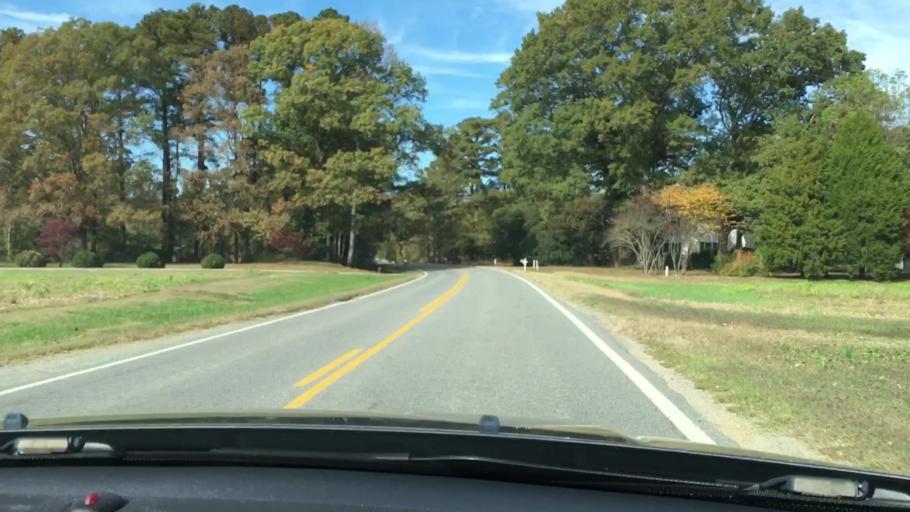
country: US
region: Virginia
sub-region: King William County
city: West Point
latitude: 37.5183
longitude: -76.8221
